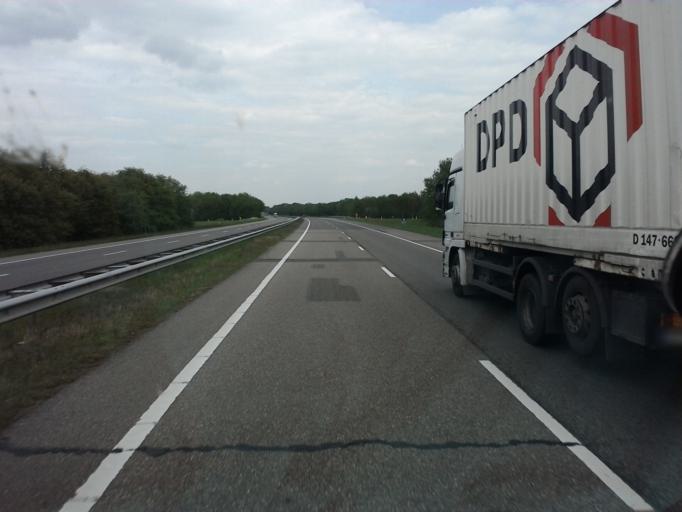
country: NL
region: Limburg
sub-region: Gemeente Gennep
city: Gennep
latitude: 51.6677
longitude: 5.9913
